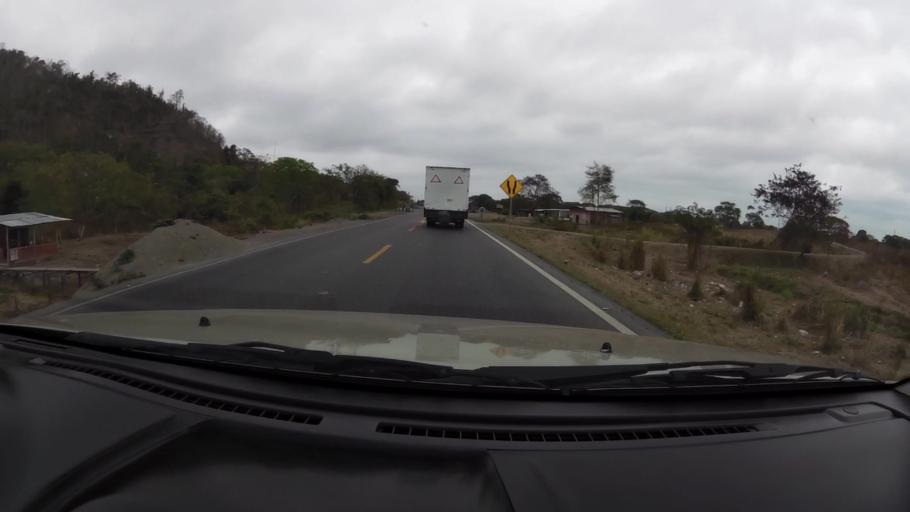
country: EC
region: Guayas
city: Naranjal
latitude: -2.4513
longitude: -79.6281
